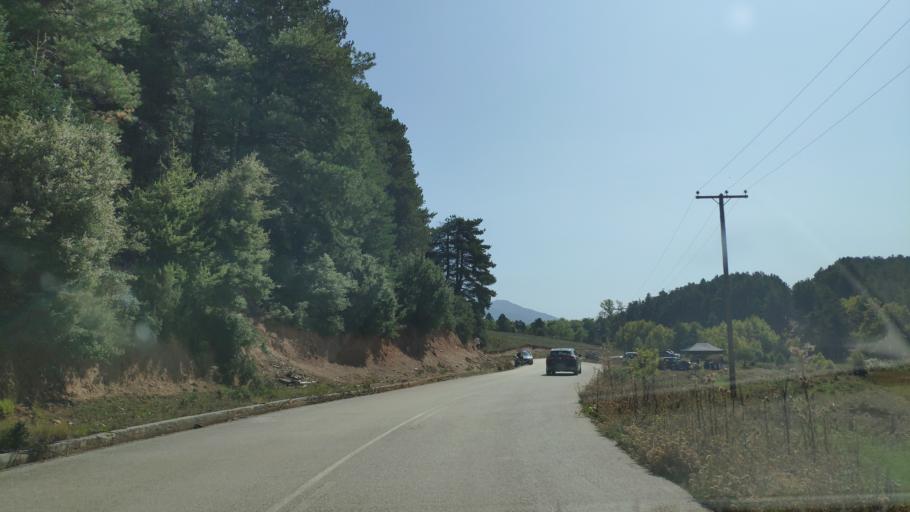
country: GR
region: West Greece
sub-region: Nomos Achaias
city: Kalavryta
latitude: 37.9267
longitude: 22.2922
